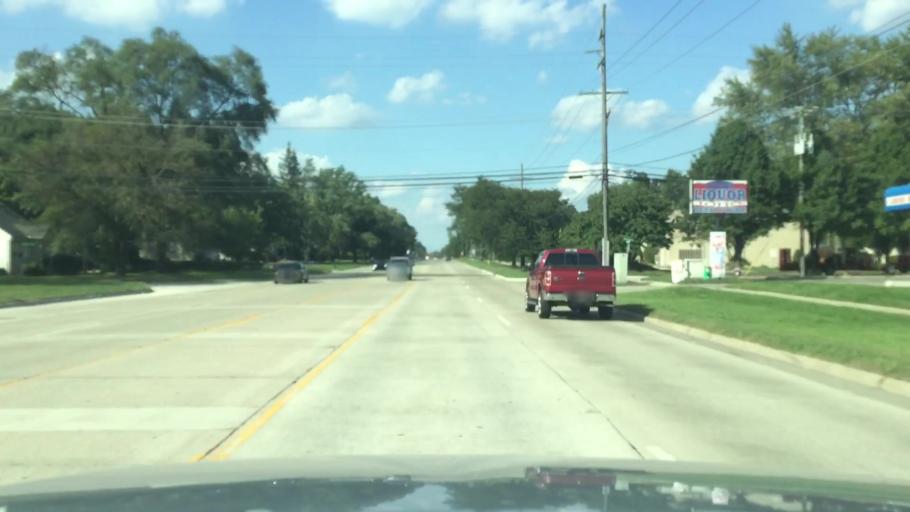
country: US
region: Michigan
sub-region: Wayne County
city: Westland
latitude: 42.3254
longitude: -83.4087
